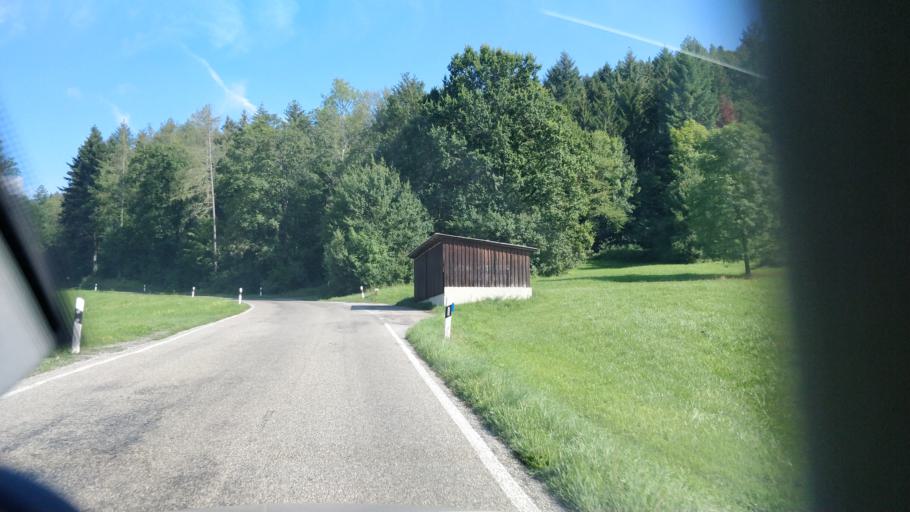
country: DE
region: Baden-Wuerttemberg
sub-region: Regierungsbezirk Stuttgart
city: Murrhardt
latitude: 48.9917
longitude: 9.5849
